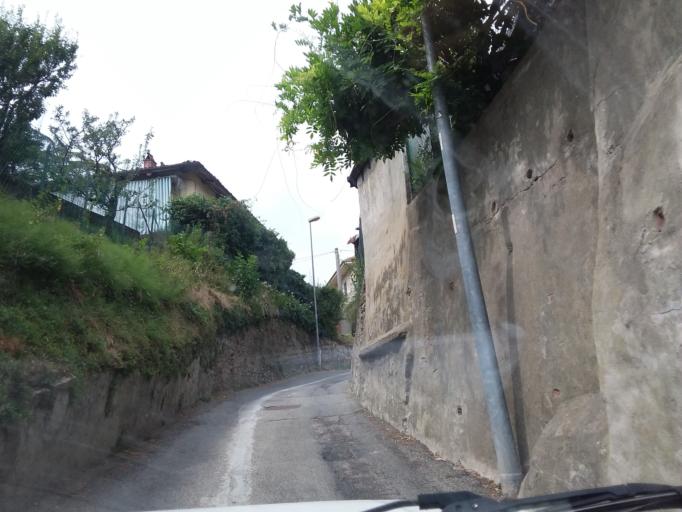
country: IT
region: Piedmont
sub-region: Provincia di Torino
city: Rivoli
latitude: 45.0655
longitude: 7.5103
